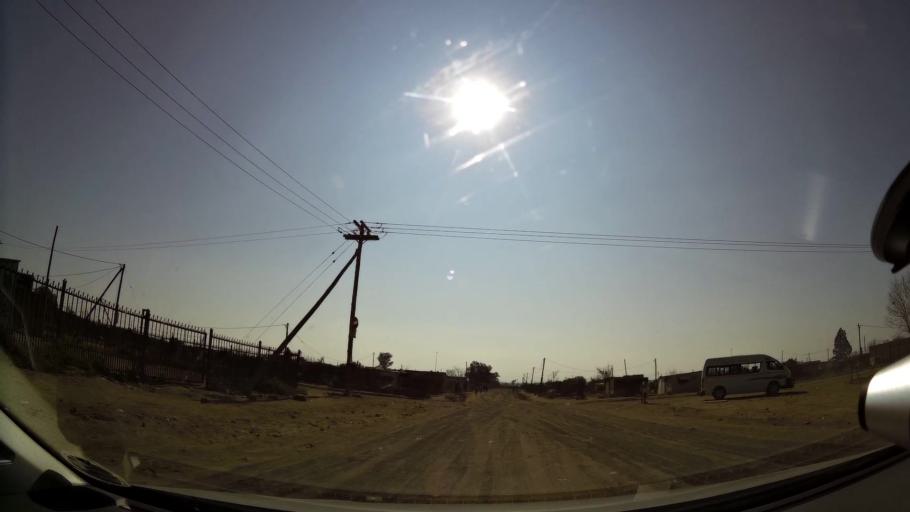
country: ZA
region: Orange Free State
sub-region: Mangaung Metropolitan Municipality
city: Bloemfontein
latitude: -29.1761
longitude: 26.2897
